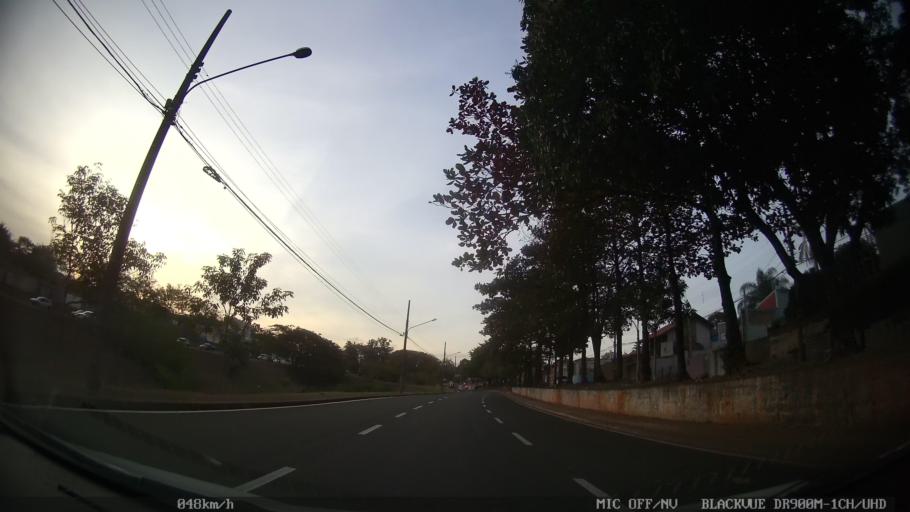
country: BR
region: Sao Paulo
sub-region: Limeira
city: Limeira
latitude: -22.5679
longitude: -47.4155
